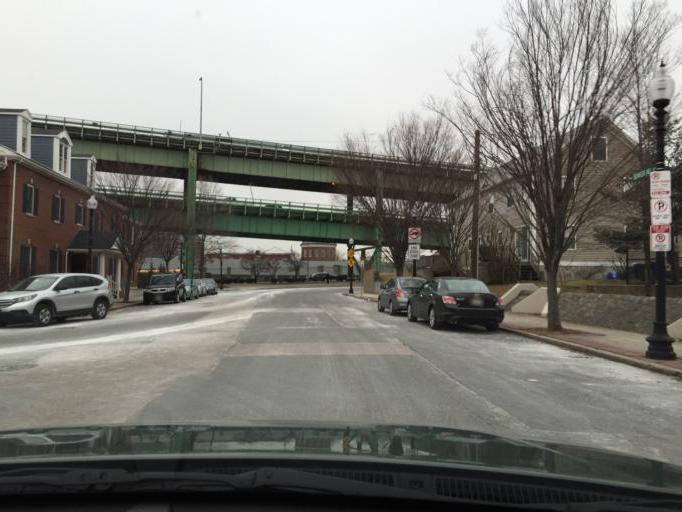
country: US
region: Massachusetts
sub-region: Suffolk County
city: Boston
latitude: 42.3764
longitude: -71.0568
